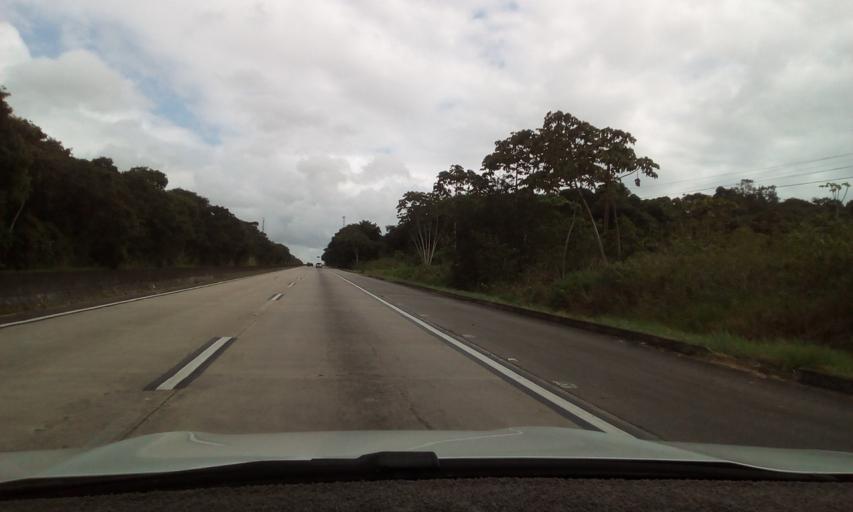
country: BR
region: Paraiba
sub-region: Santa Rita
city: Santa Rita
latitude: -7.0623
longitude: -35.0161
